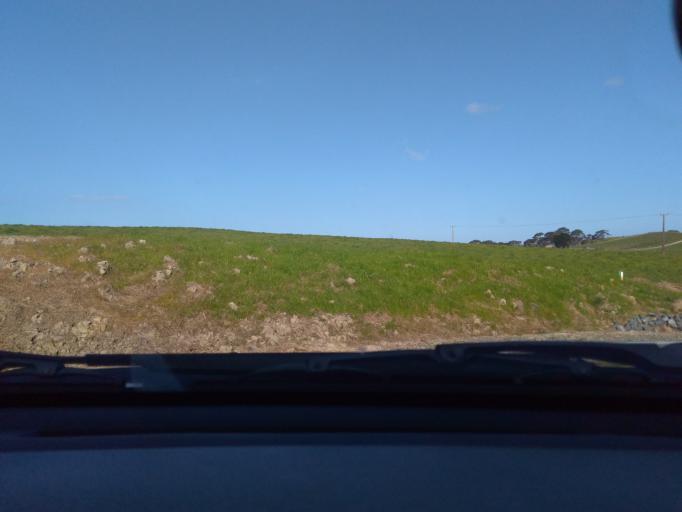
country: NZ
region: Auckland
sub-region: Auckland
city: Warkworth
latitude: -36.4387
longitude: 174.7559
